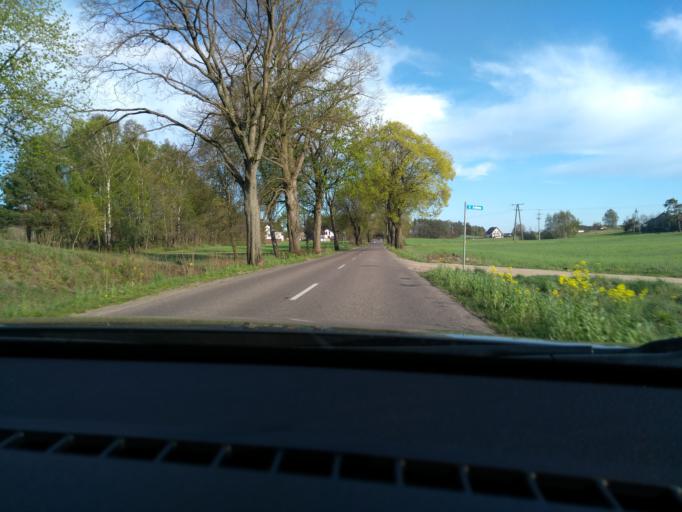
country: PL
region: Pomeranian Voivodeship
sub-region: Powiat kartuski
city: Suleczyno
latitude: 54.3333
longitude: 17.7699
